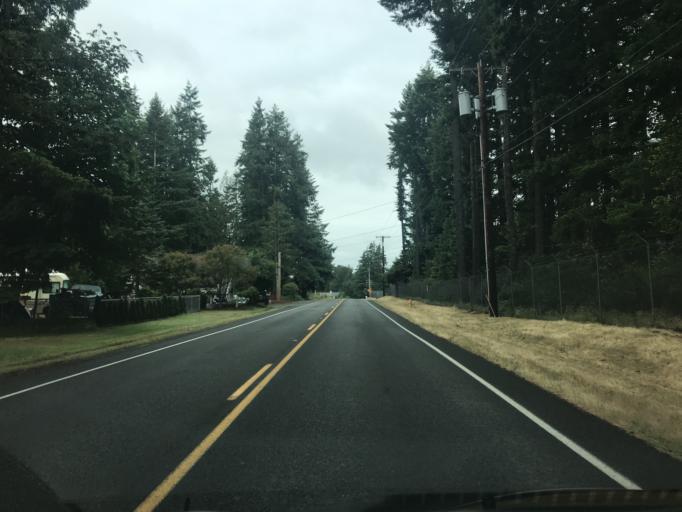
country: US
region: Washington
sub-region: King County
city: Maple Valley
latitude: 47.3436
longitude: -122.0497
